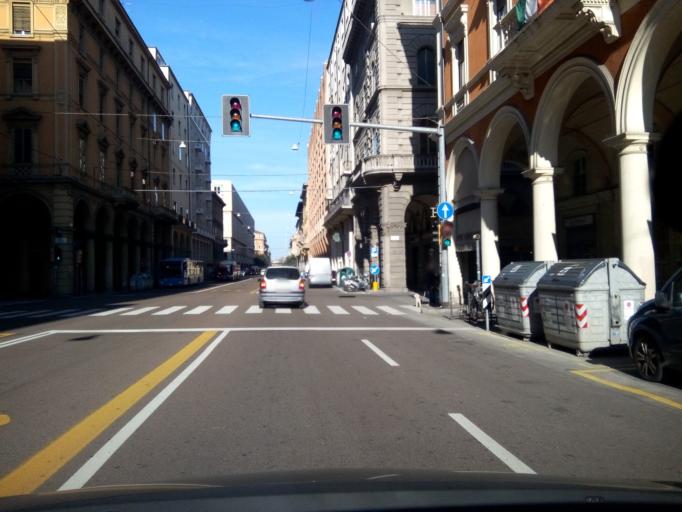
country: IT
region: Emilia-Romagna
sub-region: Provincia di Bologna
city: Bologna
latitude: 44.5013
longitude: 11.3440
